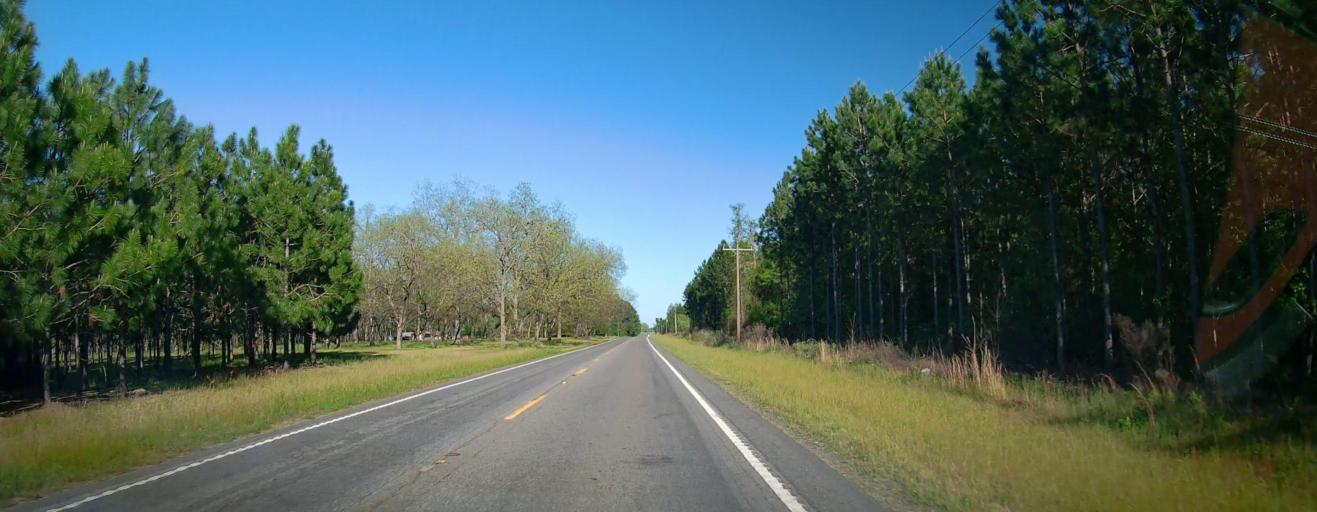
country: US
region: Georgia
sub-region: Ben Hill County
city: Fitzgerald
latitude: 31.7185
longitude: -83.3363
